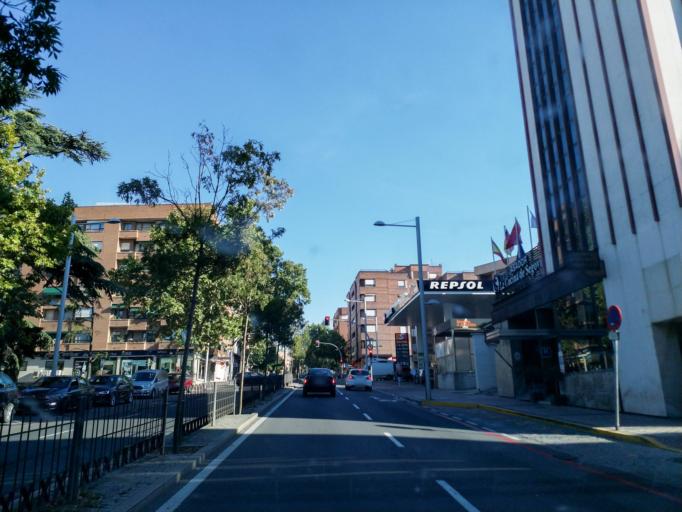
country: ES
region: Castille and Leon
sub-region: Provincia de Segovia
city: Segovia
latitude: 40.9441
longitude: -4.1207
